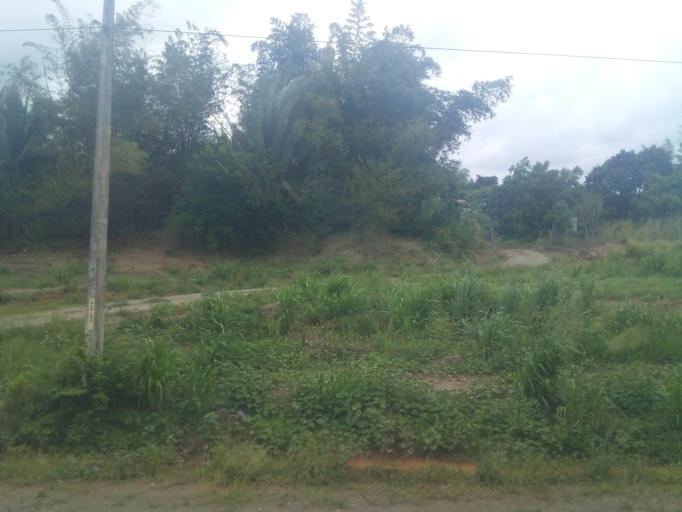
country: BR
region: Maranhao
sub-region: Santa Ines
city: Santa Ines
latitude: -3.6877
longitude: -45.3534
